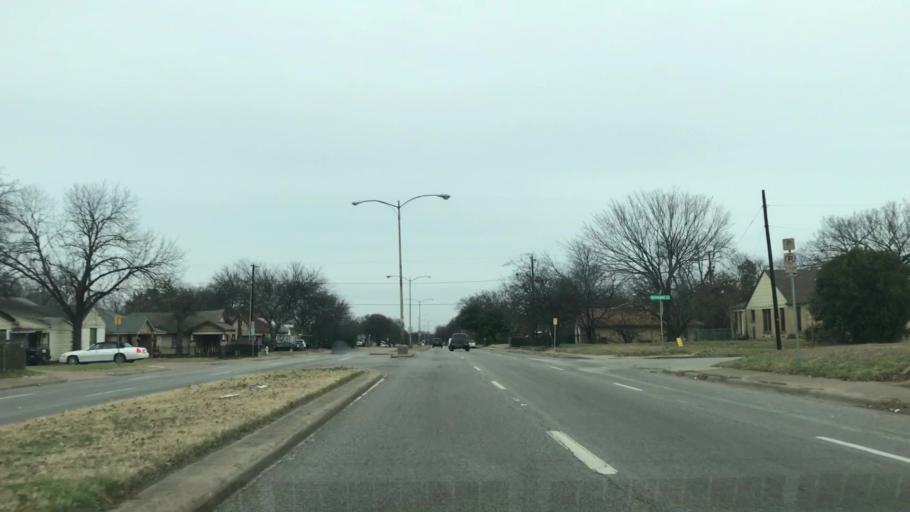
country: US
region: Texas
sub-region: Dallas County
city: Dallas
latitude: 32.7269
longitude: -96.8144
